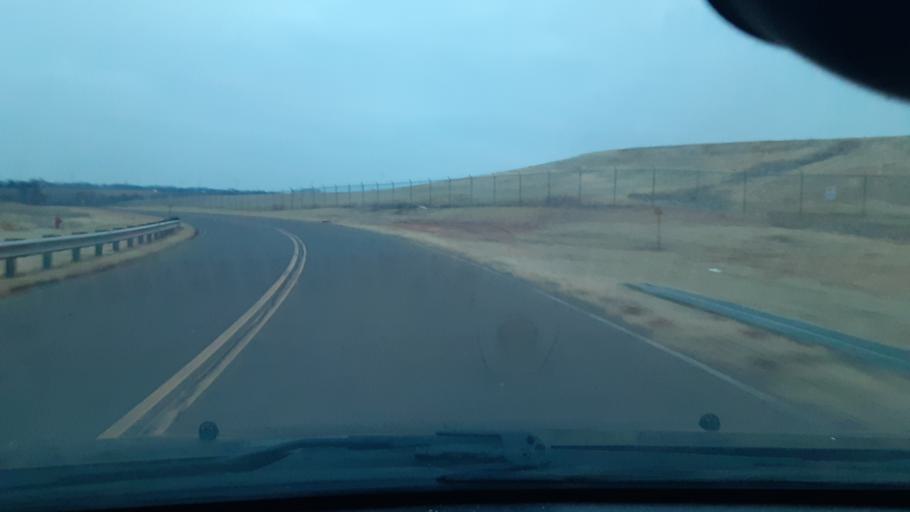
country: US
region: Oklahoma
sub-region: Logan County
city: Guthrie
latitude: 35.8571
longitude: -97.4203
